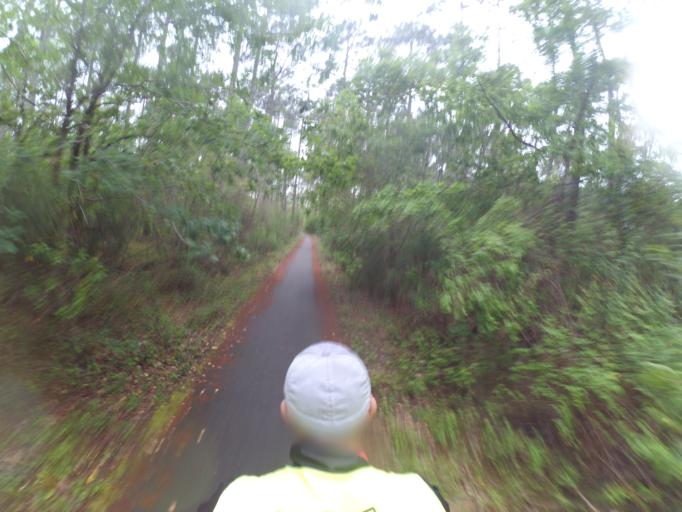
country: FR
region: Aquitaine
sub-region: Departement des Landes
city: Mimizan
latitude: 44.2192
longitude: -1.2456
